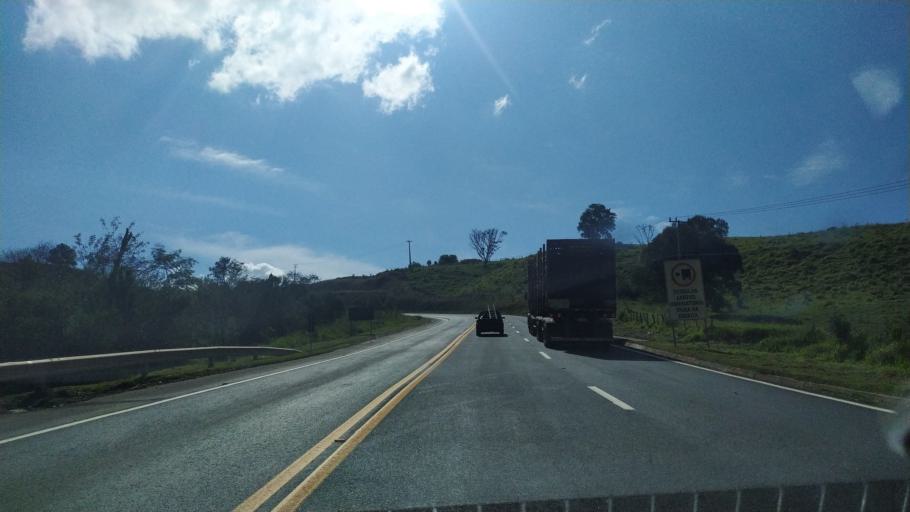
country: BR
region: Parana
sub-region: Telemaco Borba
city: Telemaco Borba
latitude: -24.2887
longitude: -50.7049
